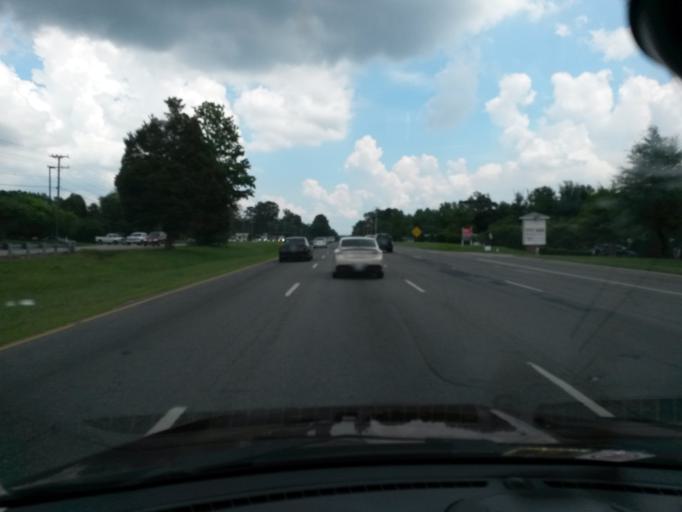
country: US
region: Virginia
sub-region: Chesterfield County
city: Enon
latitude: 37.3484
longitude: -77.3561
